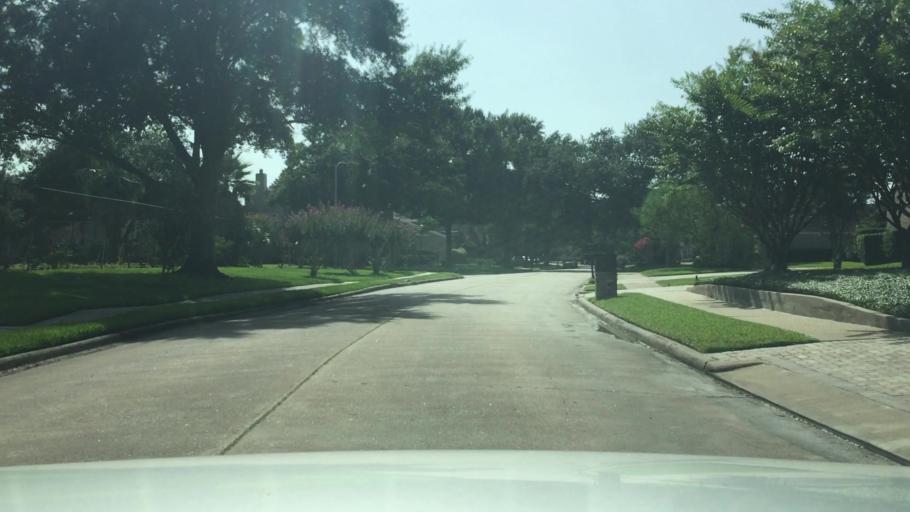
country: US
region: Texas
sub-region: Harris County
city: Bunker Hill Village
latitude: 29.7536
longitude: -95.5808
